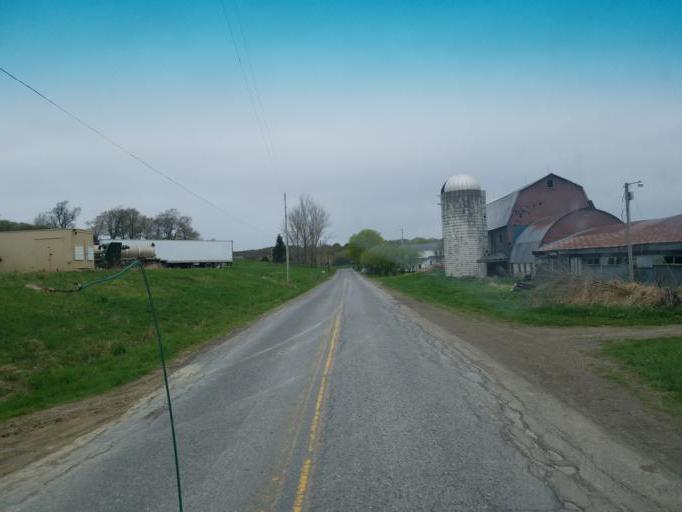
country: US
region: Pennsylvania
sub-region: Potter County
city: Galeton
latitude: 41.8892
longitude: -77.7421
